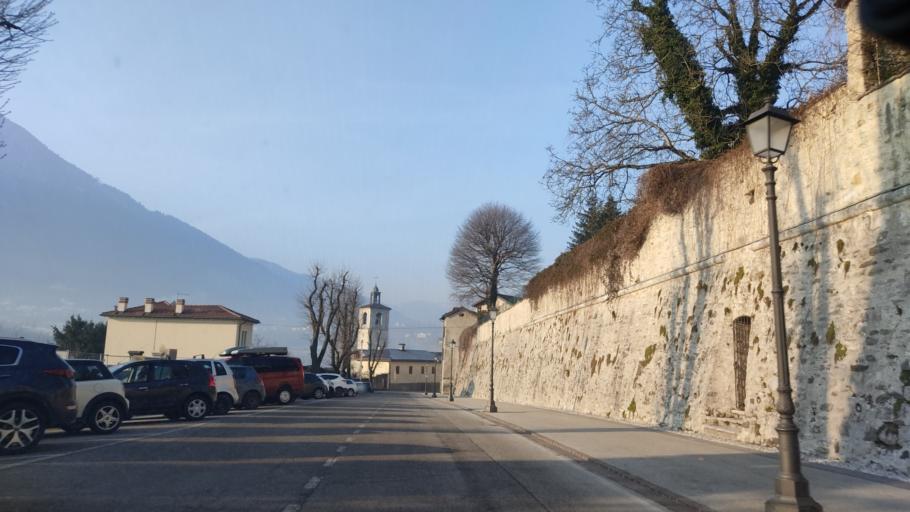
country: IT
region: Veneto
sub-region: Provincia di Belluno
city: Feltre
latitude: 46.0180
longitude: 11.9119
